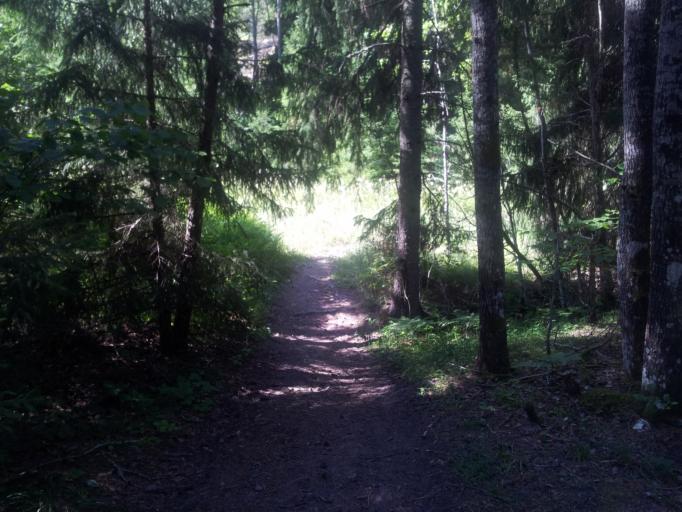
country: SE
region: Stockholm
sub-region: Norrtalje Kommun
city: Nykvarn
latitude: 59.8986
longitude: 18.2512
